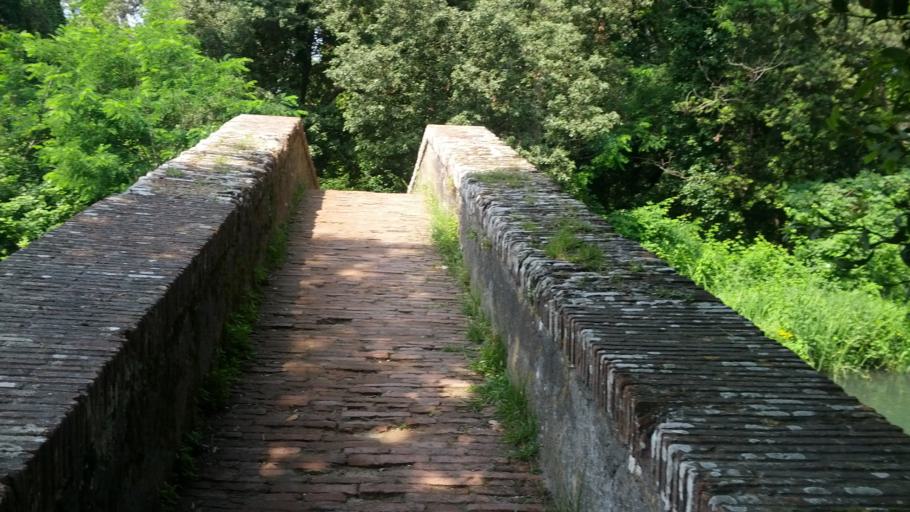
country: IT
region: Tuscany
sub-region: Provincia di Lucca
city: Pietrasanta
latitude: 43.9390
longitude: 10.1931
